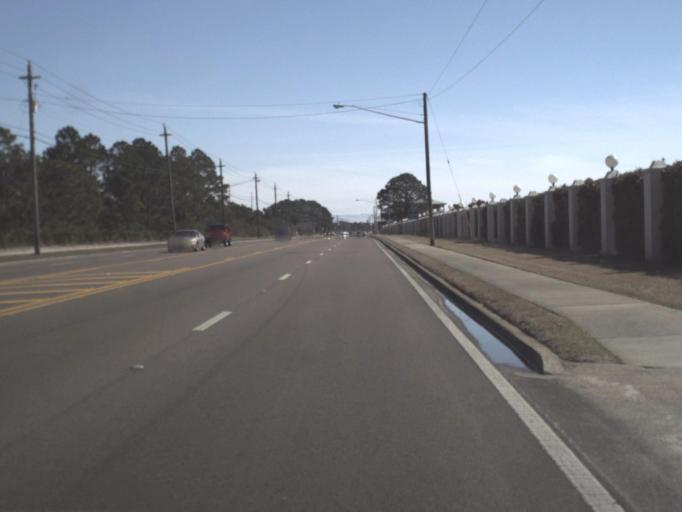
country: US
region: Florida
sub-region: Bay County
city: Panama City Beach
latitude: 30.1911
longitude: -85.8215
